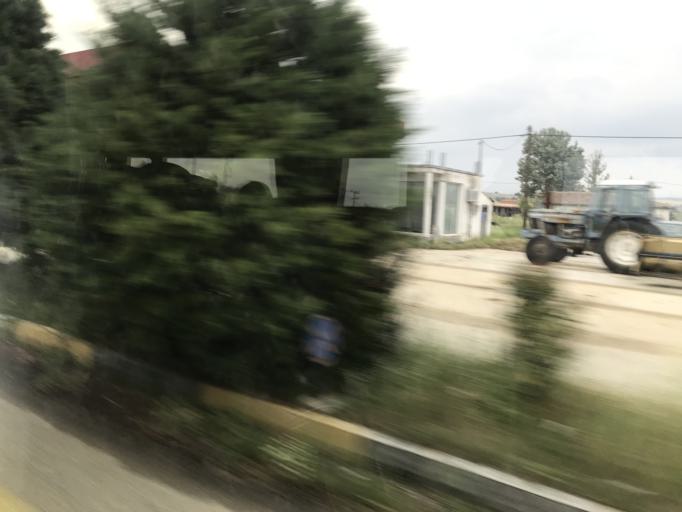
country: GR
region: East Macedonia and Thrace
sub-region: Nomos Rodopis
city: Aratos
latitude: 41.0839
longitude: 25.5398
